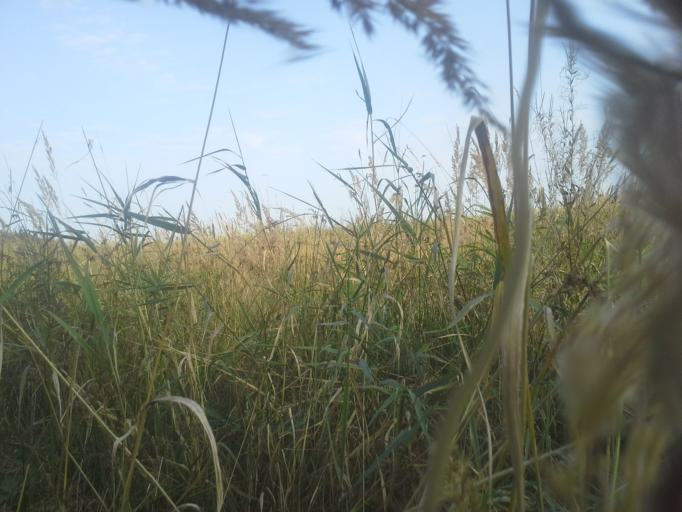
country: RU
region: Moskovskaya
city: Kievskij
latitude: 55.3832
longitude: 36.9236
